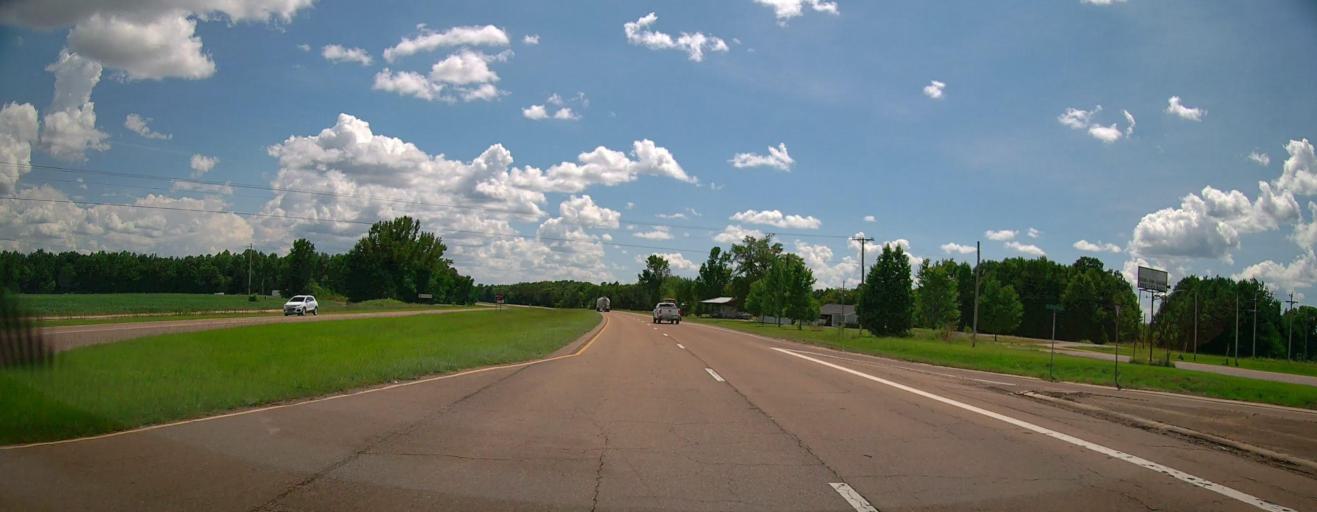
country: US
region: Mississippi
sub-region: Lowndes County
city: Columbus Air Force Base
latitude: 33.7253
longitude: -88.4457
